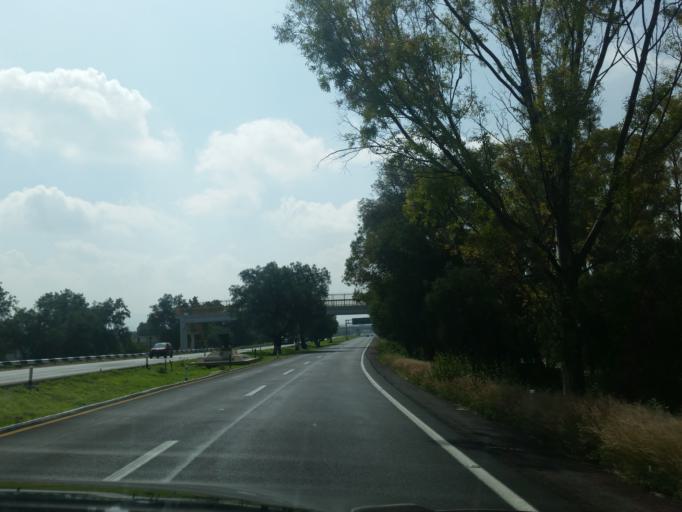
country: MX
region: Mexico
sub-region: Acolman de Nezahualcoyotl
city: Prados de San Juan
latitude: 19.6206
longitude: -98.9612
